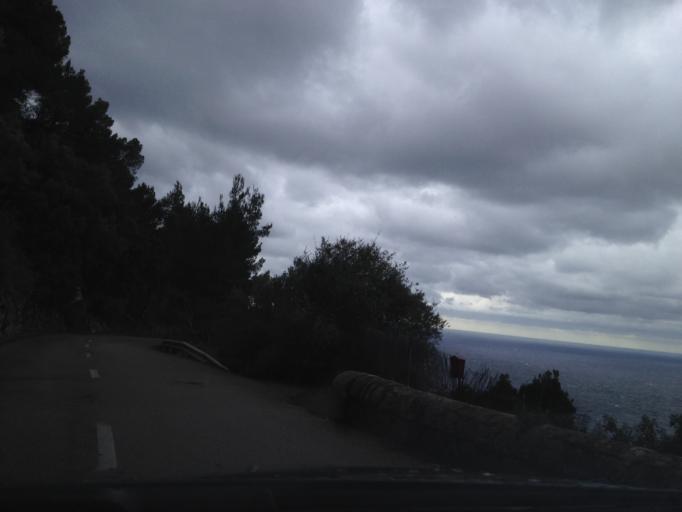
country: ES
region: Balearic Islands
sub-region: Illes Balears
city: Deia
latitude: 39.7738
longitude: 2.6712
